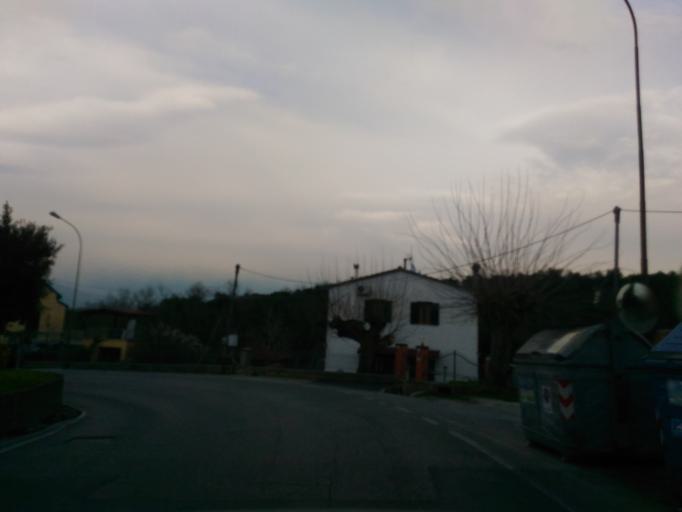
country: IT
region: Tuscany
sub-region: Provincia di Livorno
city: Collesalvetti
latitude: 43.5905
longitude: 10.4770
